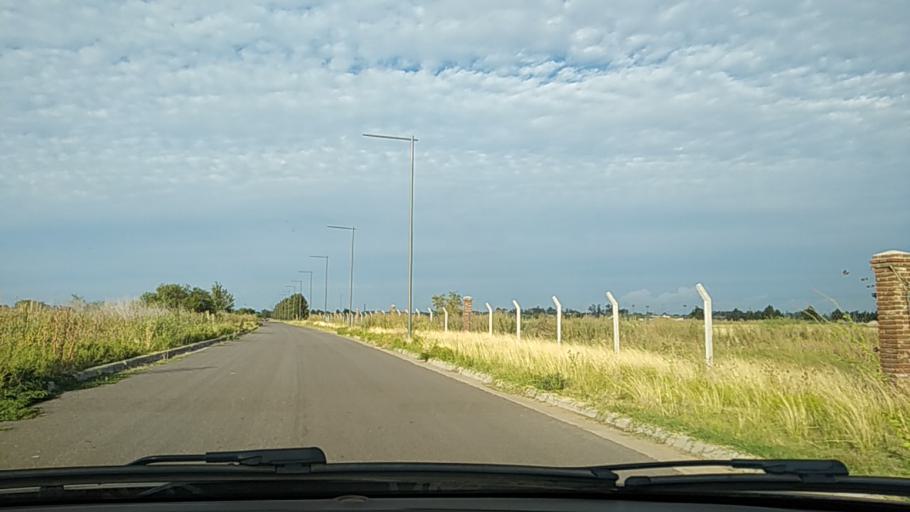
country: AR
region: Santa Fe
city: Funes
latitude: -32.9429
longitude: -60.7747
